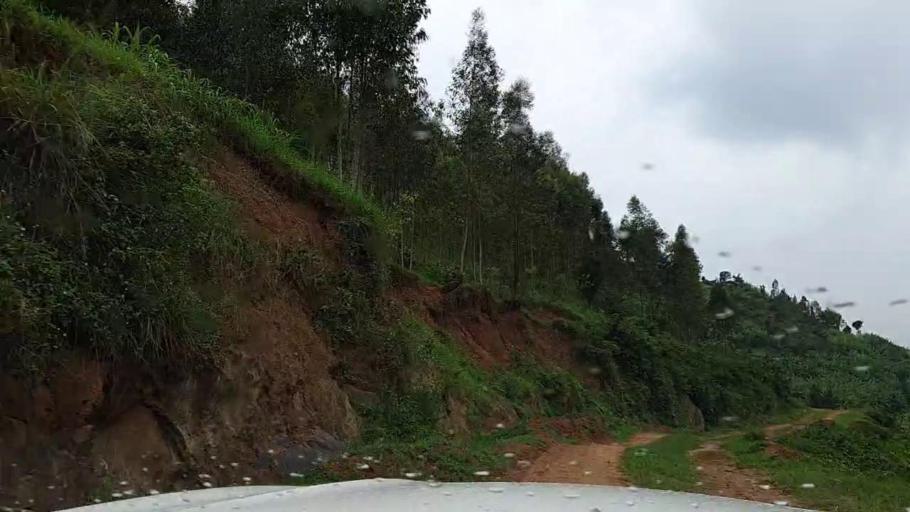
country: RW
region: Kigali
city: Kigali
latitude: -1.9063
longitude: 29.9575
